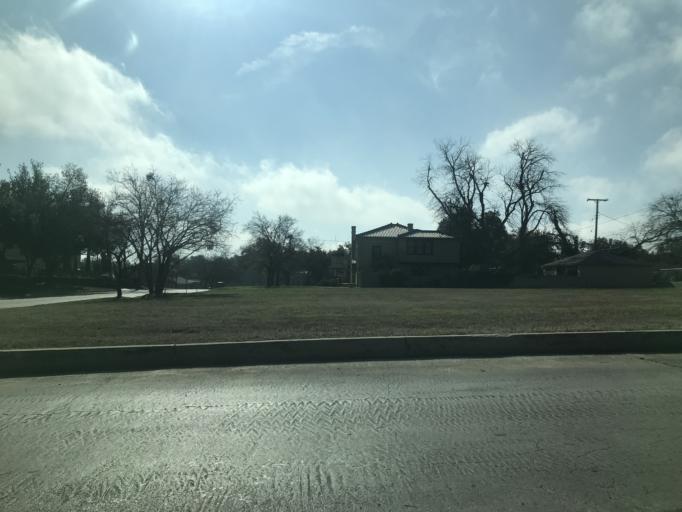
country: US
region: Texas
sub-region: Tom Green County
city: San Angelo
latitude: 31.4539
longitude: -100.4500
